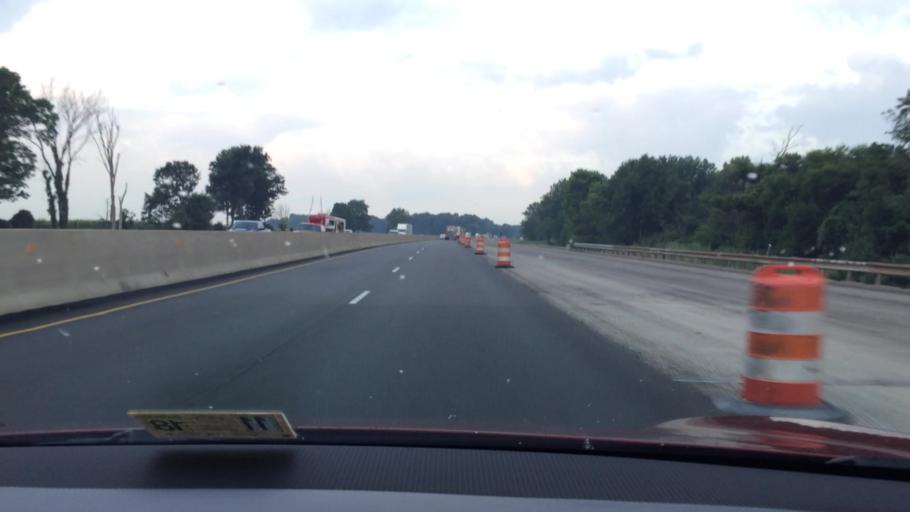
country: US
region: Ohio
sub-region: Lorain County
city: South Amherst
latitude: 41.3505
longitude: -82.3092
